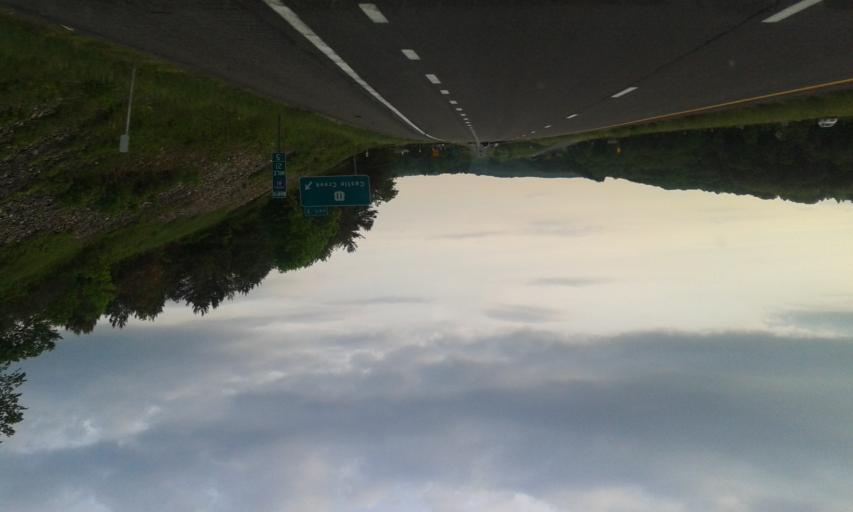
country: US
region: New York
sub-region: Broome County
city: Chenango Bridge
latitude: 42.2291
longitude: -75.9138
